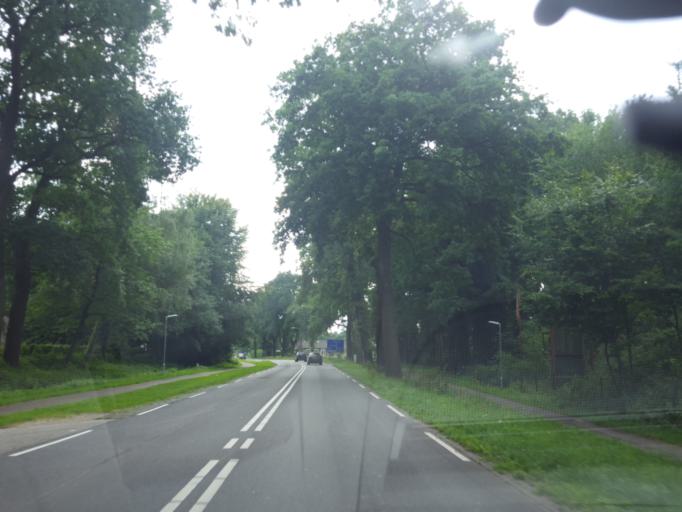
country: NL
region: Limburg
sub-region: Gemeente Bergen
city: Wellerlooi
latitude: 51.4713
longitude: 6.0593
